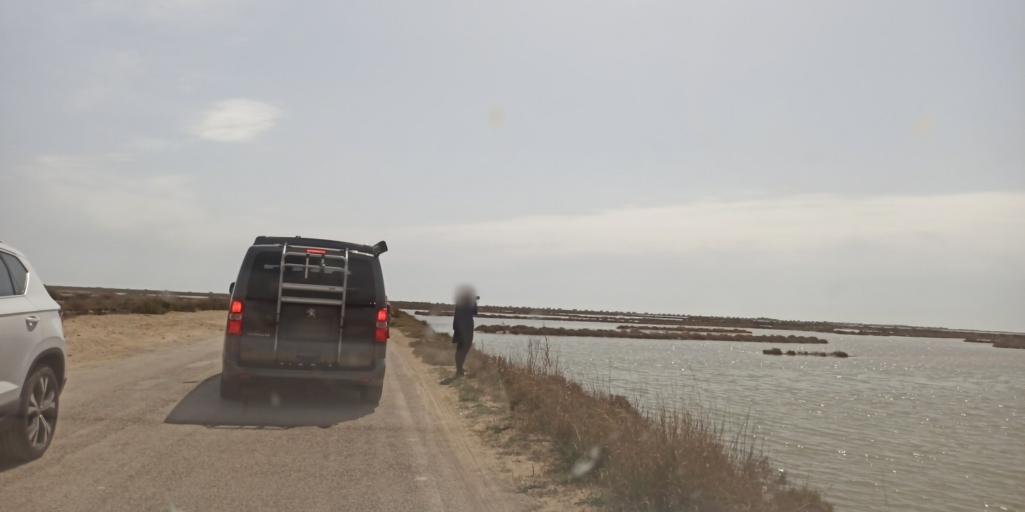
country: ES
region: Catalonia
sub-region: Provincia de Tarragona
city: Deltebre
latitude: 40.6417
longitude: 0.7381
